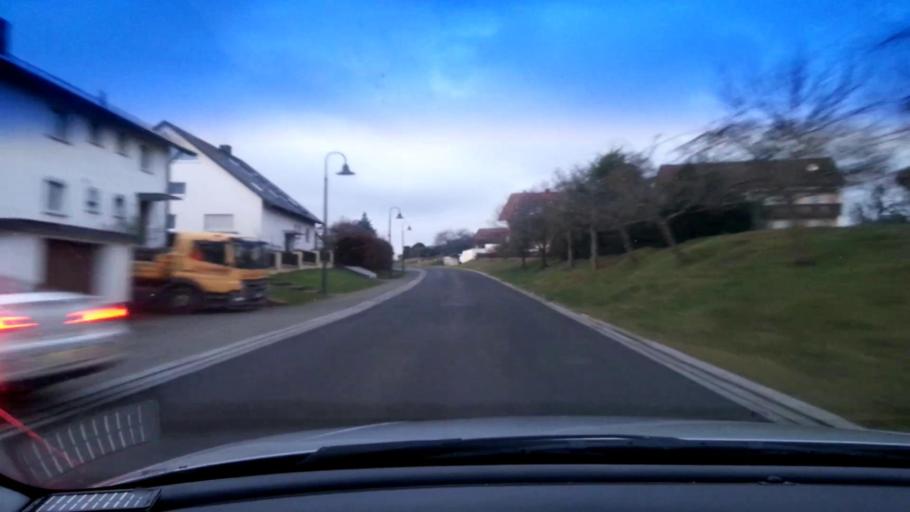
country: DE
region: Bavaria
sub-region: Upper Franconia
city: Frensdorf
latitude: 49.8249
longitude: 10.8868
